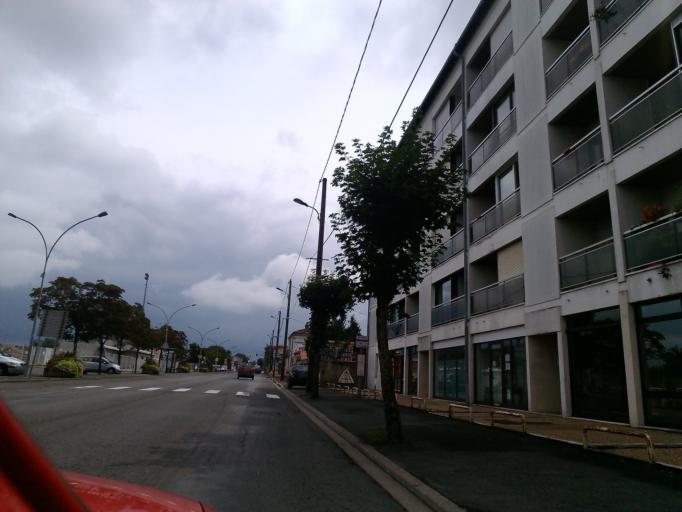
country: FR
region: Poitou-Charentes
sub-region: Departement de la Charente
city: Cognac
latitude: 45.6885
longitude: -0.3149
